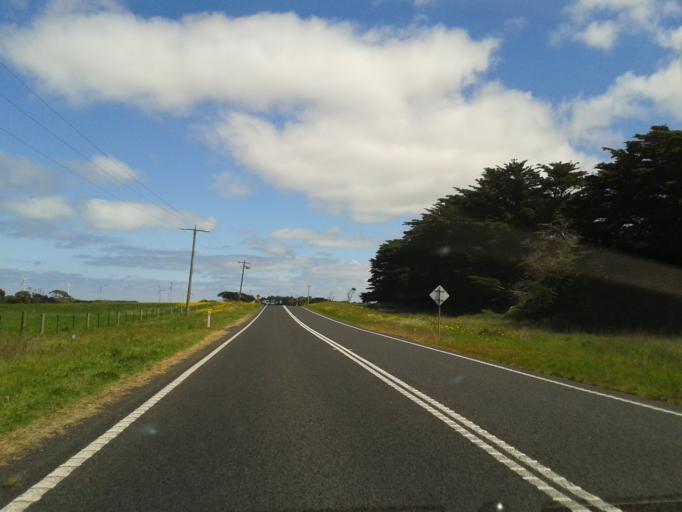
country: AU
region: Victoria
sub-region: Moyne
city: Port Fairy
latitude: -38.3124
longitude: 142.0594
